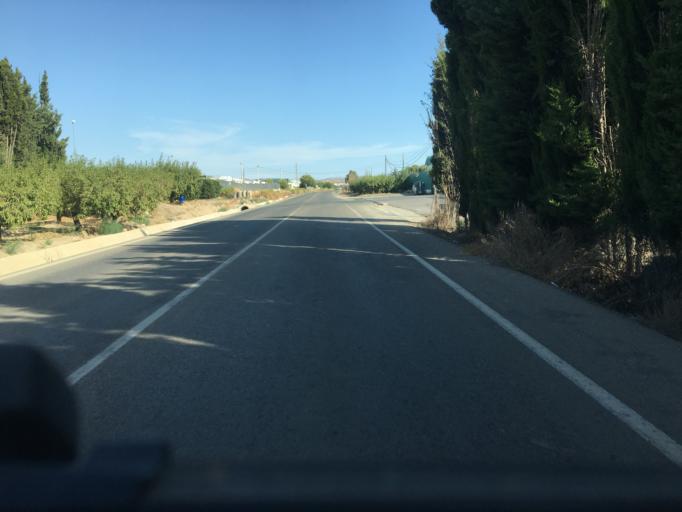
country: ES
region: Andalusia
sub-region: Provincia de Almeria
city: Huercal-Overa
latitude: 37.4099
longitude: -1.9607
